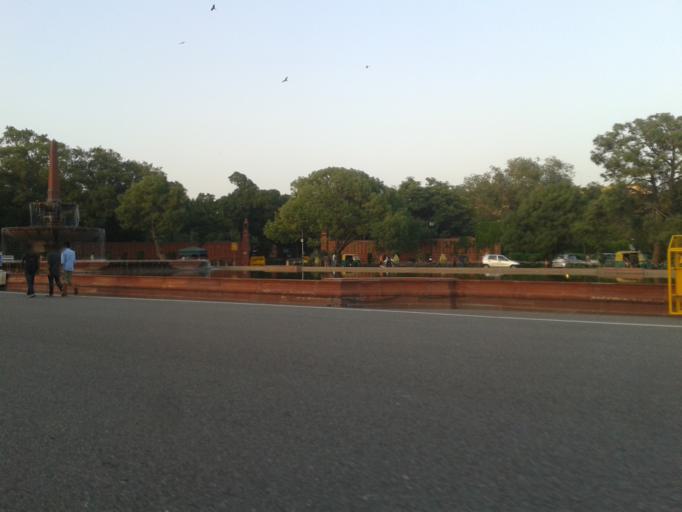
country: IN
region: NCT
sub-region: New Delhi
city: New Delhi
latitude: 28.6151
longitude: 77.2088
